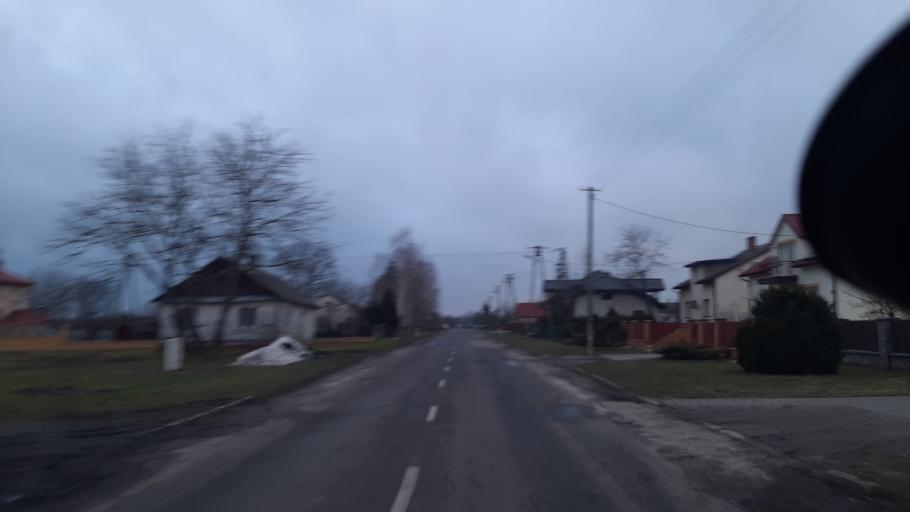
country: PL
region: Lublin Voivodeship
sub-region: Powiat parczewski
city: Debowa Kloda
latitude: 51.6197
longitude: 23.0939
